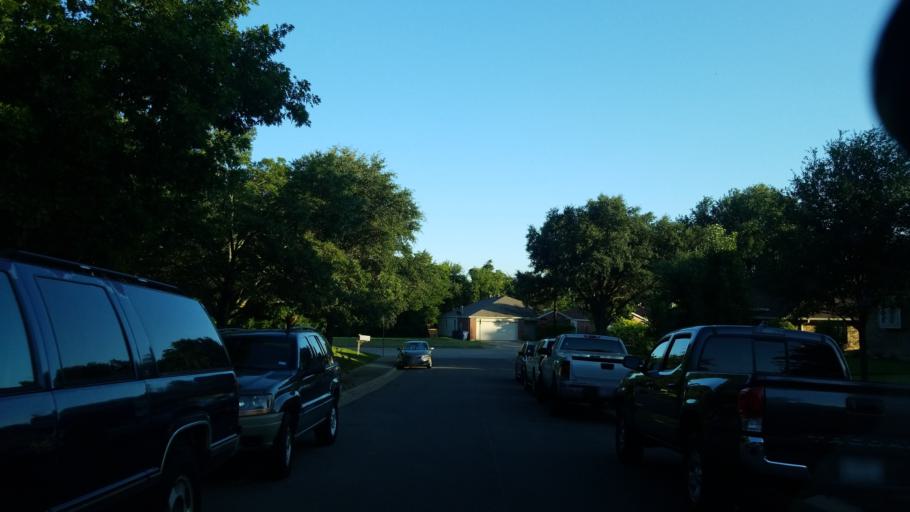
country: US
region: Texas
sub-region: Dallas County
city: Balch Springs
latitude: 32.7864
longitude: -96.6954
